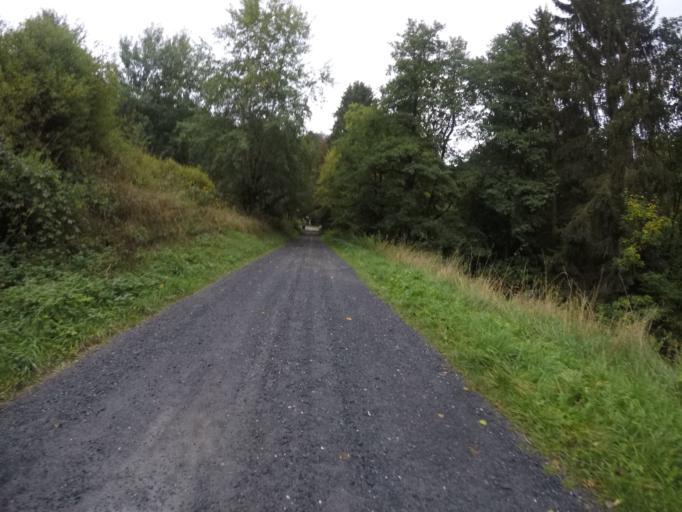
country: BE
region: Wallonia
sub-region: Province du Luxembourg
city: Fauvillers
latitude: 49.8552
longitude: 5.6995
